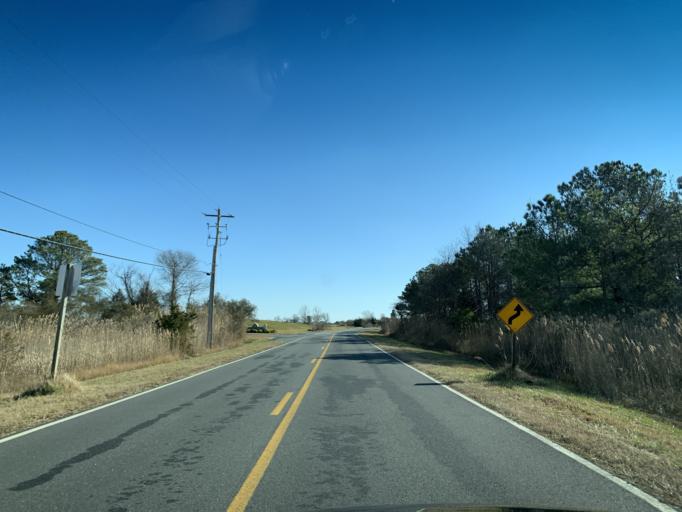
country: US
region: Maryland
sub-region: Worcester County
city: Ocean Pines
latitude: 38.4109
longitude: -75.1112
